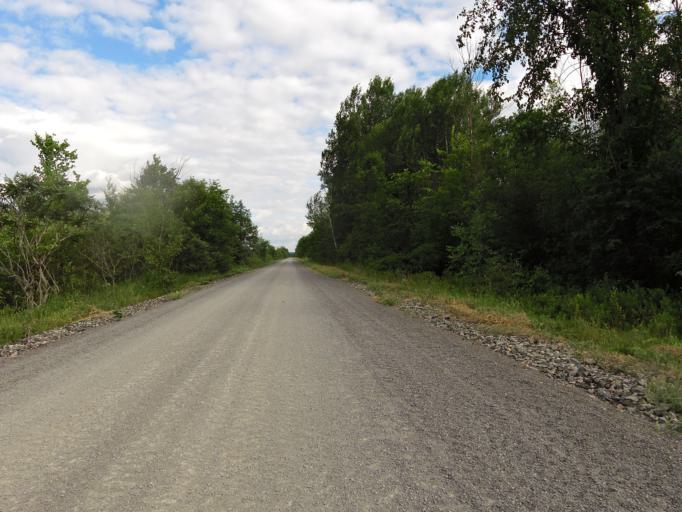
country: CA
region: Ontario
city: Arnprior
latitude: 45.2943
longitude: -76.2594
